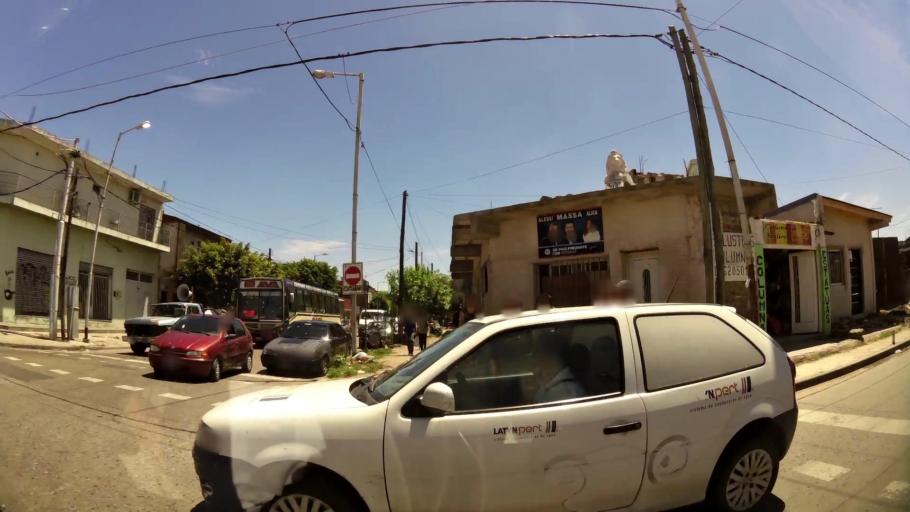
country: AR
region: Buenos Aires
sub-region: Partido de Quilmes
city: Quilmes
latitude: -34.7163
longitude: -58.3221
